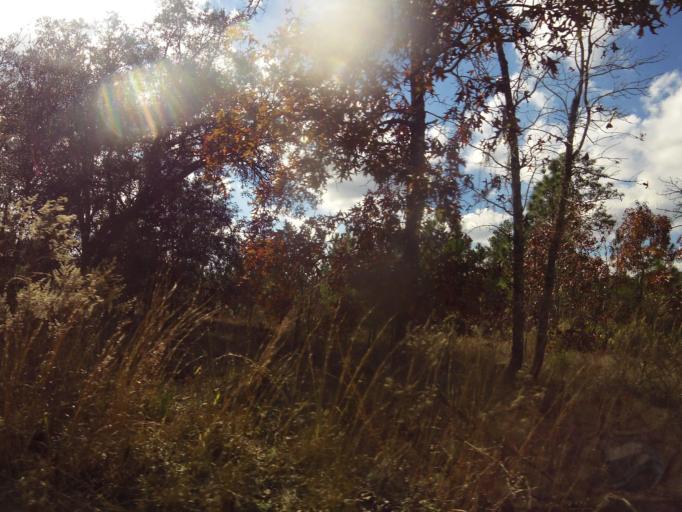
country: US
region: Florida
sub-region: Clay County
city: Middleburg
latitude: 30.1194
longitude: -81.9277
